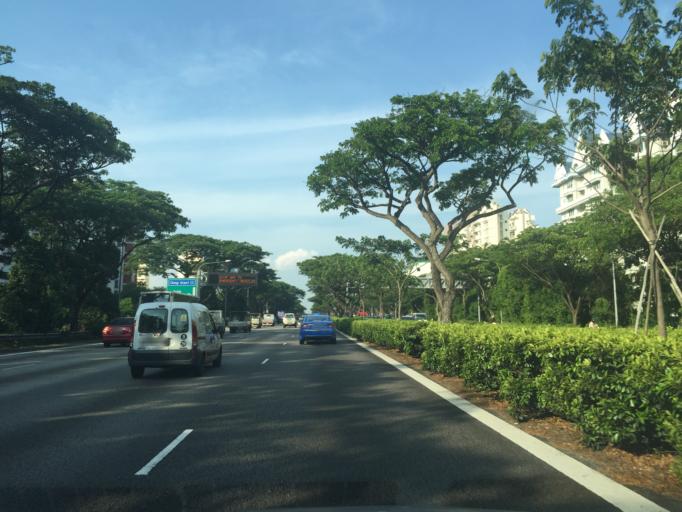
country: SG
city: Singapore
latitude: 1.3292
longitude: 103.9126
